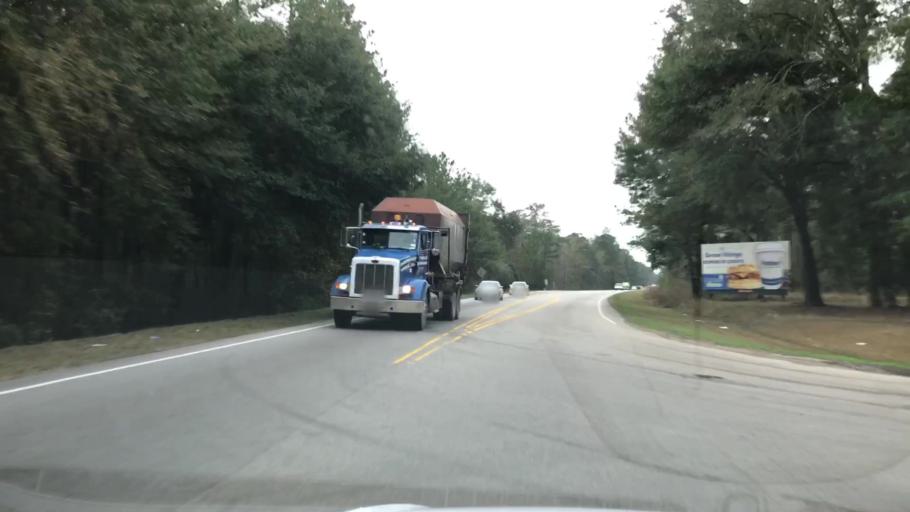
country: US
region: South Carolina
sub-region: Jasper County
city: Ridgeland
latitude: 32.3869
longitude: -80.9081
